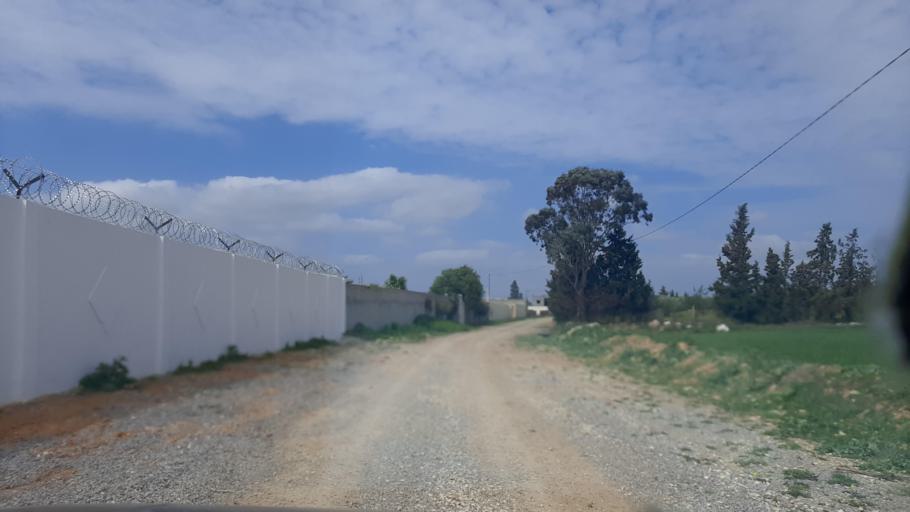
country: TN
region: Tunis
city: Oued Lill
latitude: 36.6859
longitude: 10.0006
